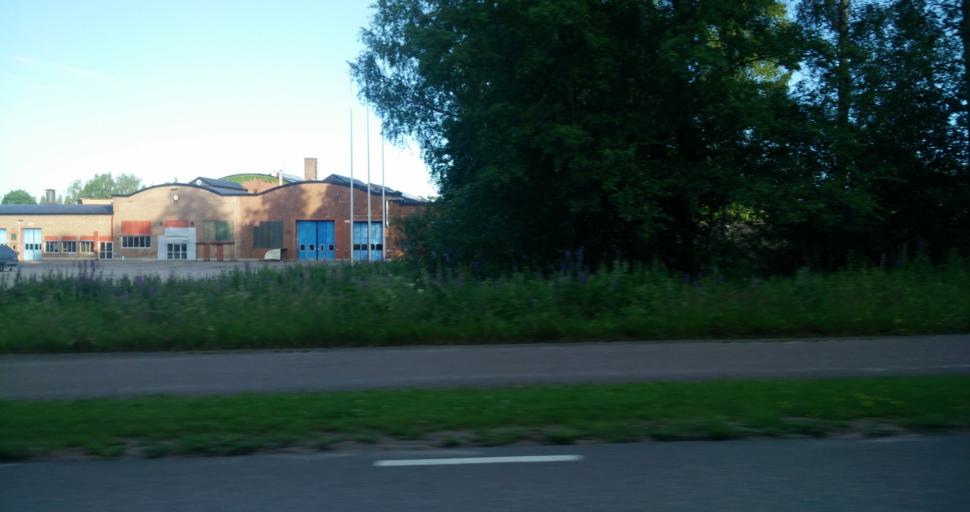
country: SE
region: Vaermland
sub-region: Hagfors Kommun
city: Hagfors
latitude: 60.0239
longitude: 13.6930
